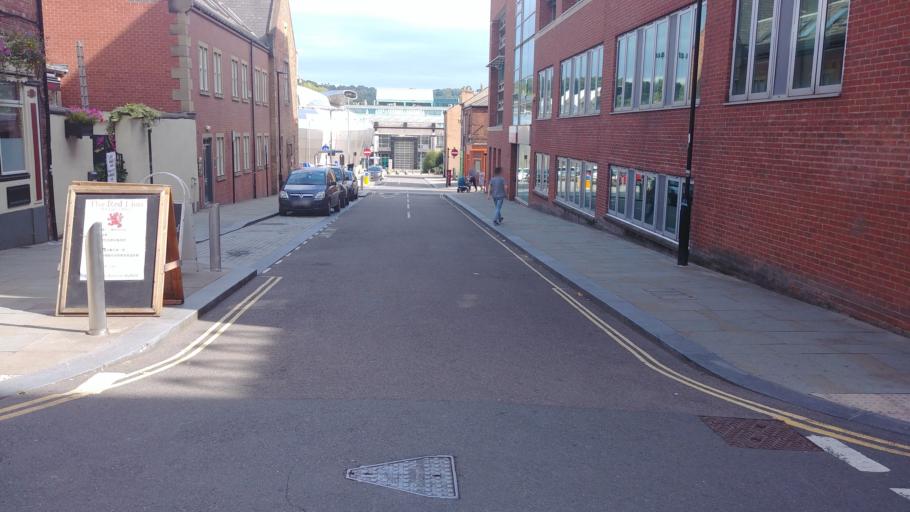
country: GB
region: England
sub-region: Sheffield
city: Sheffield
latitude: 53.3781
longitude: -1.4682
